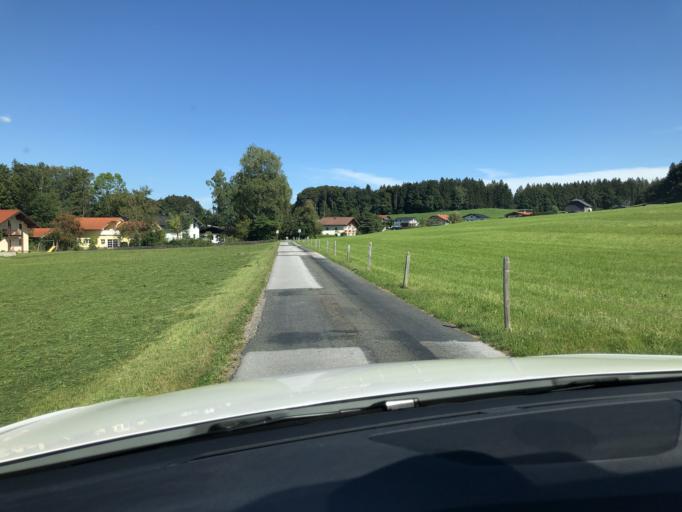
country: AT
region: Salzburg
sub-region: Politischer Bezirk Salzburg-Umgebung
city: Plainfeld
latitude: 47.8277
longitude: 13.1850
